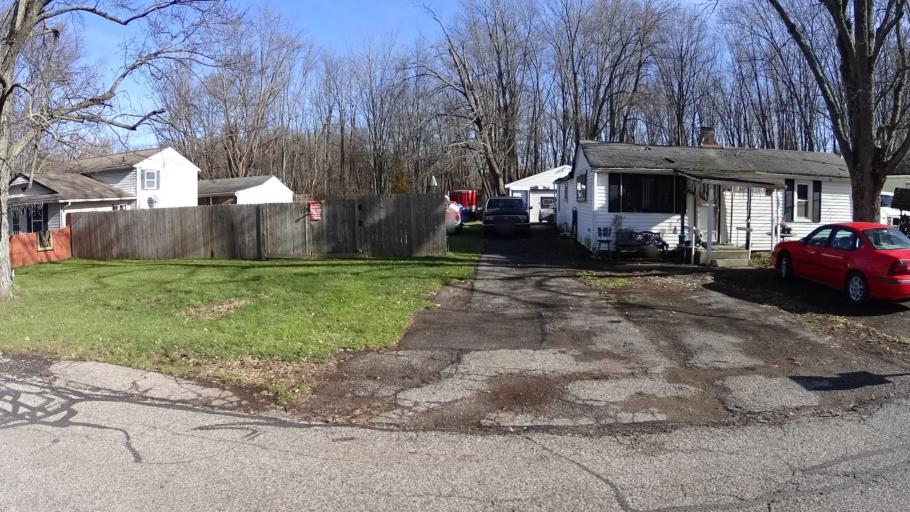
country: US
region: Ohio
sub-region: Lorain County
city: North Ridgeville
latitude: 41.4060
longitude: -81.9869
